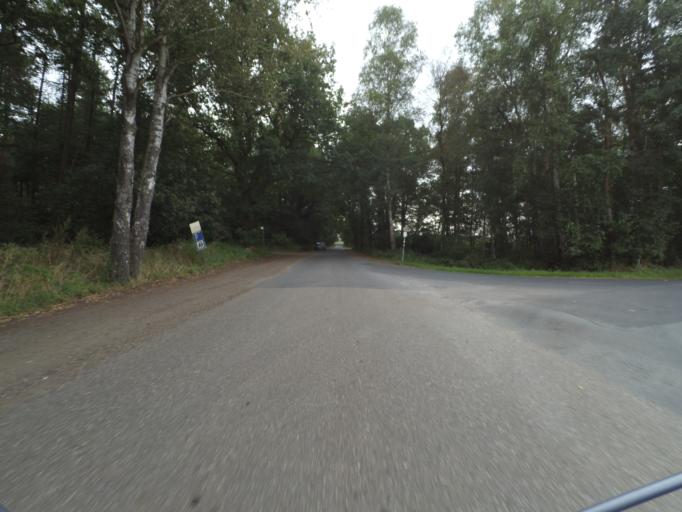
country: NL
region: Overijssel
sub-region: Gemeente Losser
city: Losser
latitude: 52.2772
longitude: 7.0484
